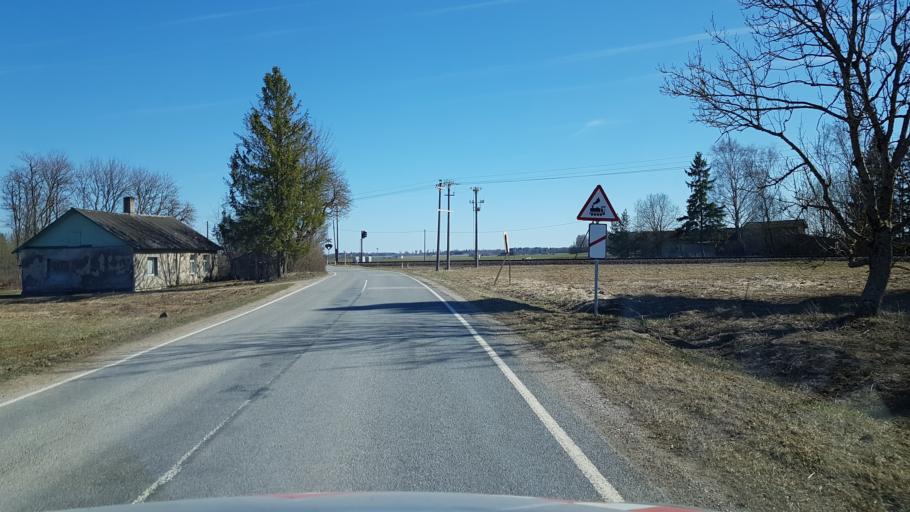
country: EE
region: Laeaene-Virumaa
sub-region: Someru vald
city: Someru
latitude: 59.3507
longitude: 26.4847
